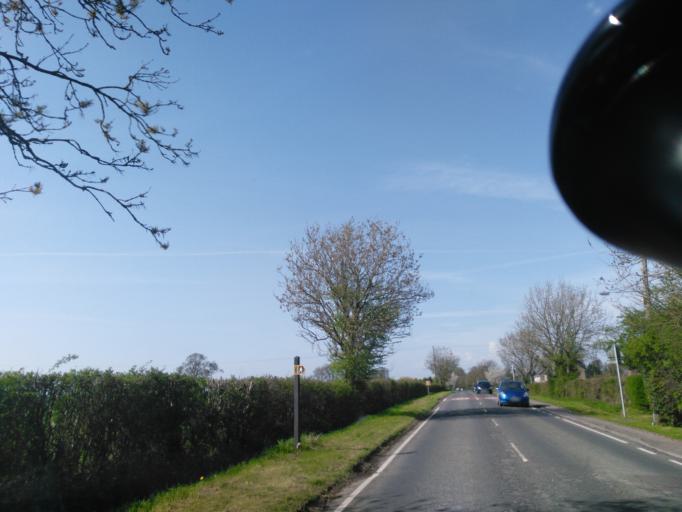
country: GB
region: England
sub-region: Wiltshire
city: Wingfield
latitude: 51.3106
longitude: -2.2571
